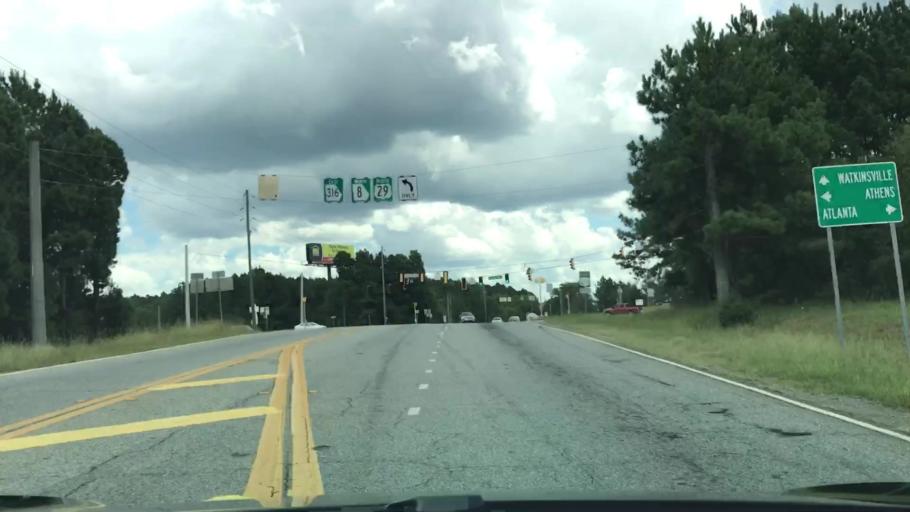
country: US
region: Georgia
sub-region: Barrow County
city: Russell
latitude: 33.9566
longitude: -83.6570
